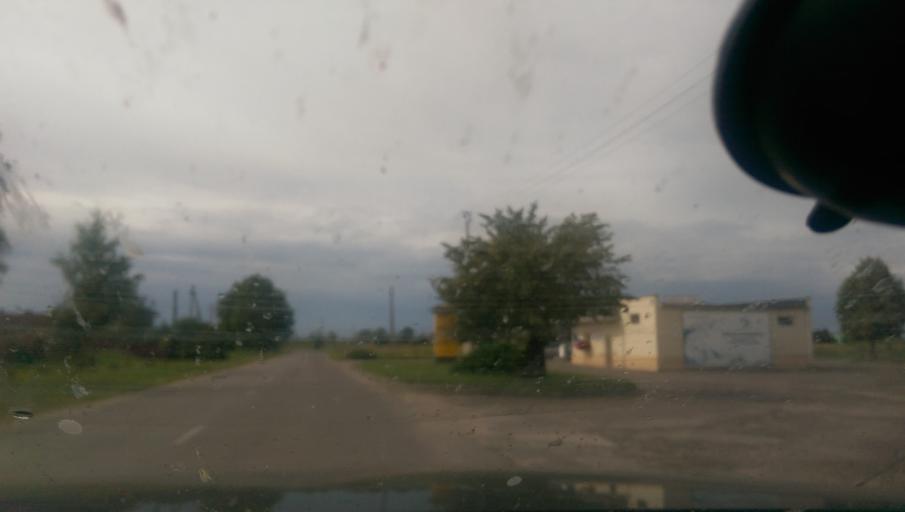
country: LT
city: Rusne
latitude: 55.2934
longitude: 21.3727
